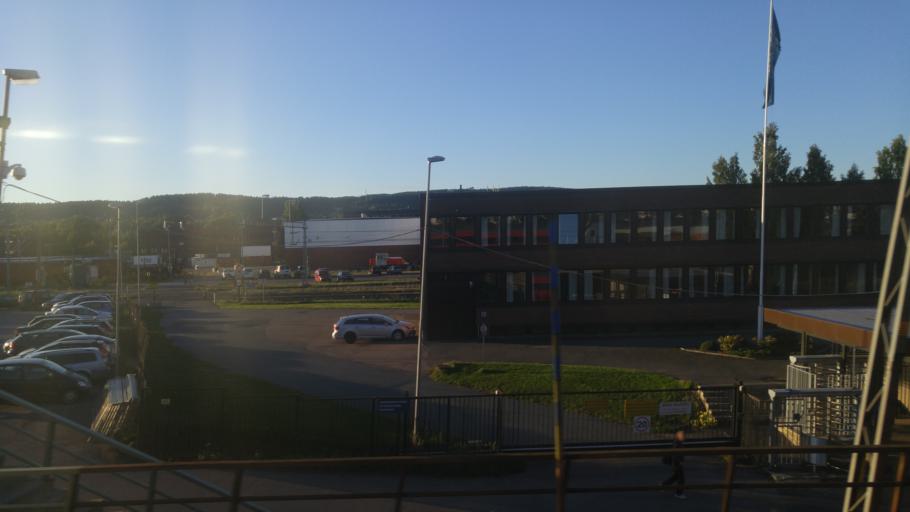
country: NO
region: Akershus
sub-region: Lorenskog
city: Kjenn
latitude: 59.9436
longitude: 10.8704
